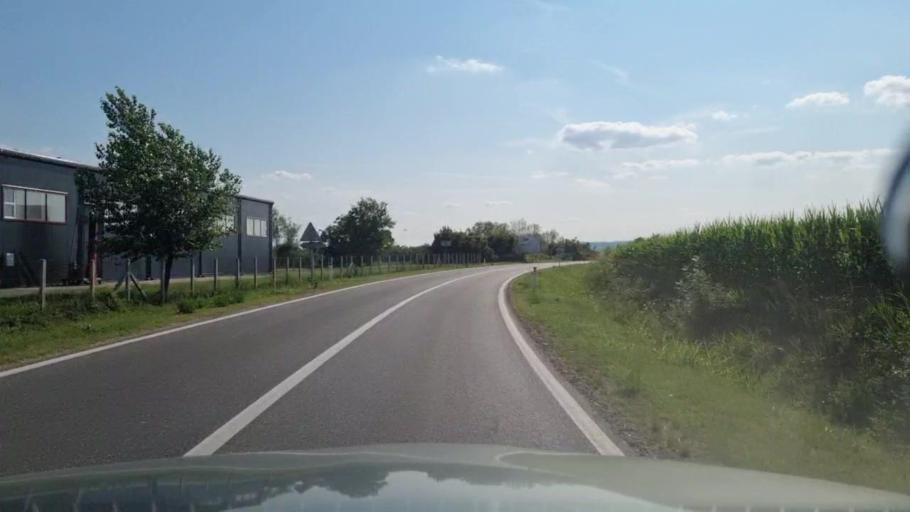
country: BA
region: Federation of Bosnia and Herzegovina
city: Odzak
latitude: 44.9954
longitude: 18.3224
